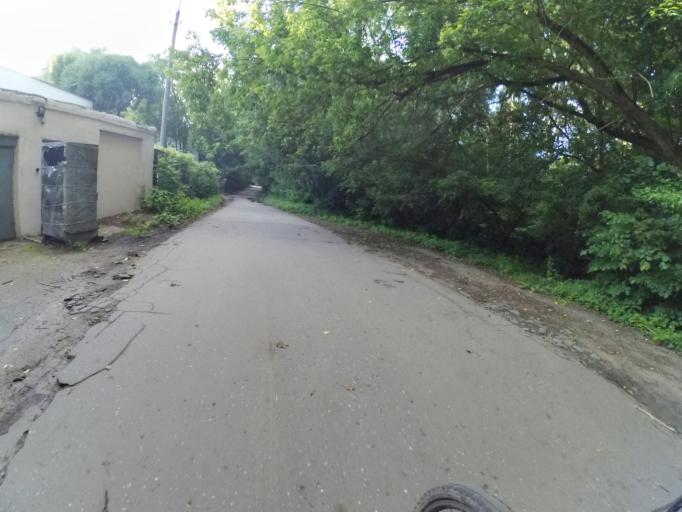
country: RU
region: Moscow
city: Strogino
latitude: 55.8352
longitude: 37.4272
